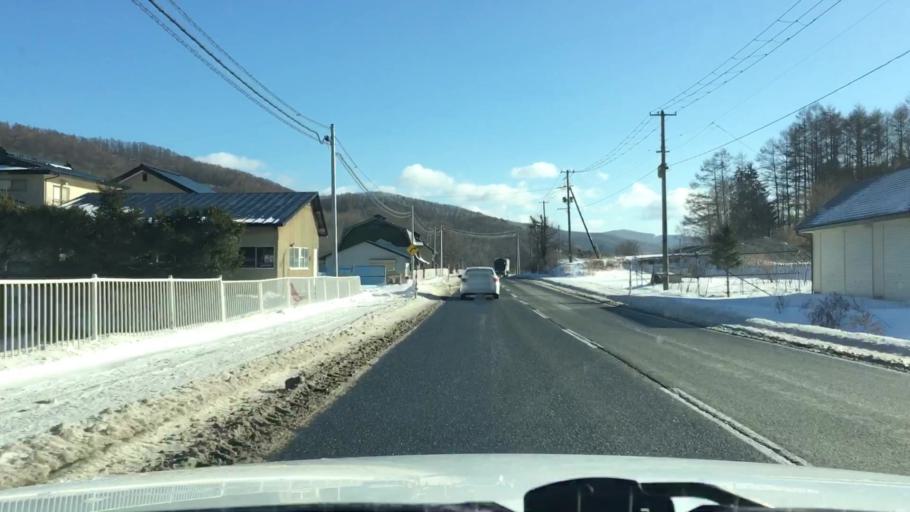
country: JP
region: Iwate
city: Morioka-shi
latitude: 39.6435
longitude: 141.3897
